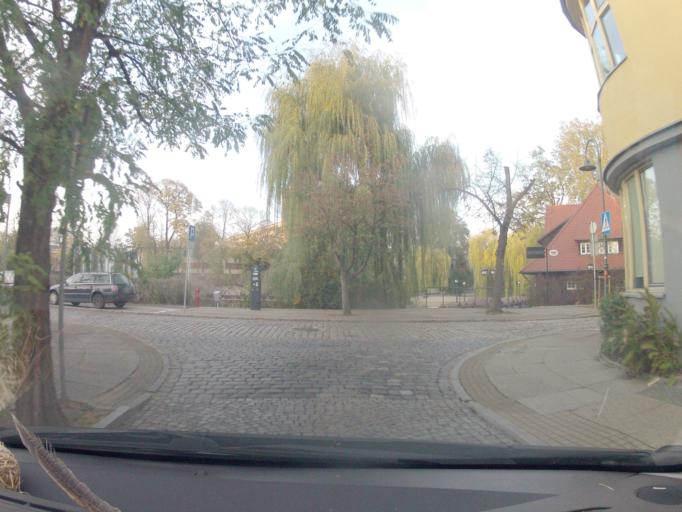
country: PL
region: Opole Voivodeship
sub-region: Powiat opolski
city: Opole
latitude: 50.6657
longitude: 17.9202
